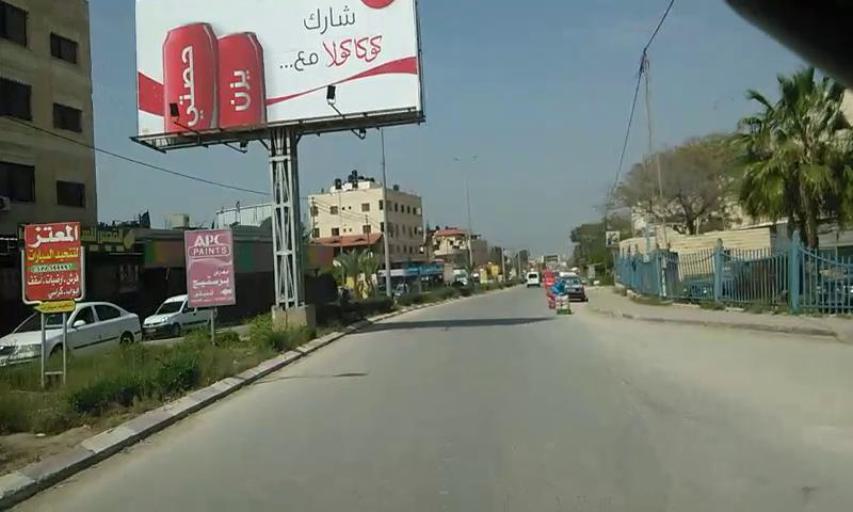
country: PS
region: West Bank
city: Janin
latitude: 32.4678
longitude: 35.3052
